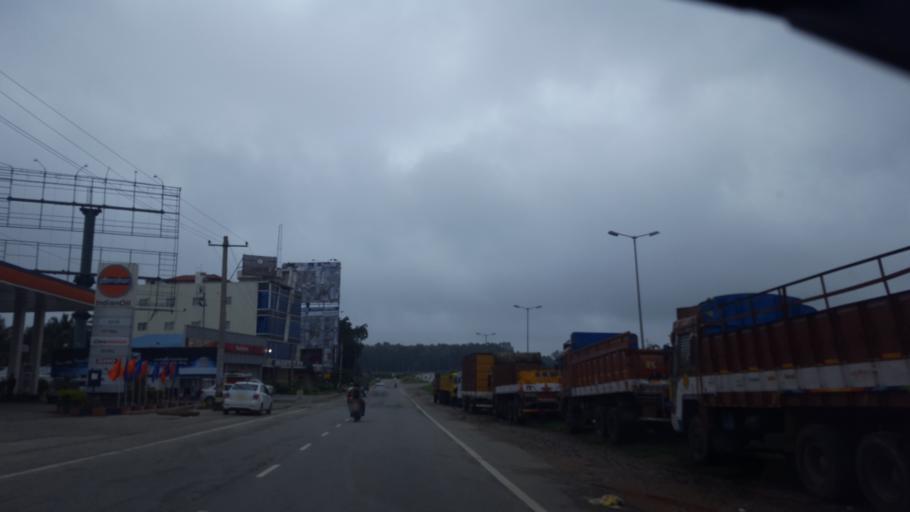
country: IN
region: Karnataka
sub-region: Bangalore Urban
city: Yelahanka
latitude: 13.1410
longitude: 77.6177
